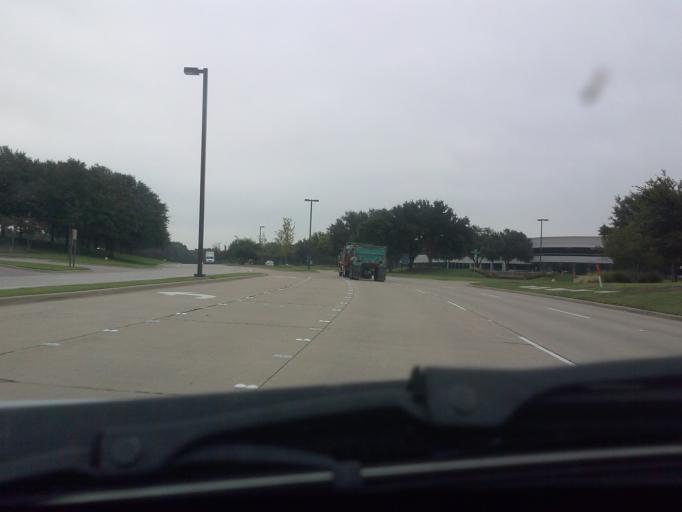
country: US
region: Texas
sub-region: Denton County
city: The Colony
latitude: 33.0707
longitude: -96.8166
